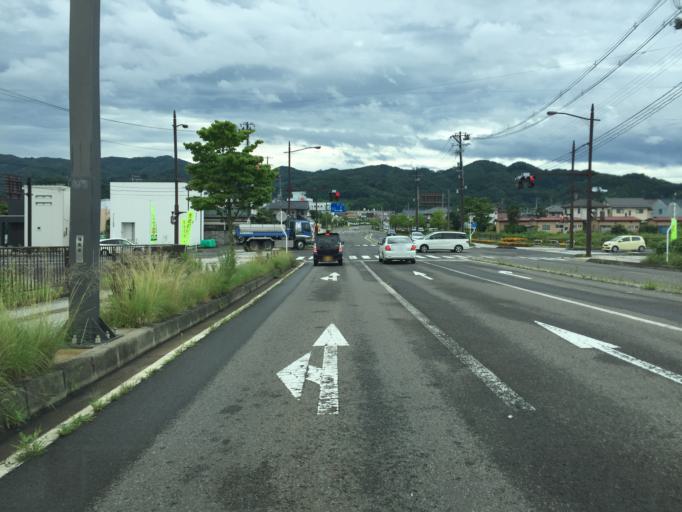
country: JP
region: Fukushima
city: Fukushima-shi
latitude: 37.7514
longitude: 140.4813
